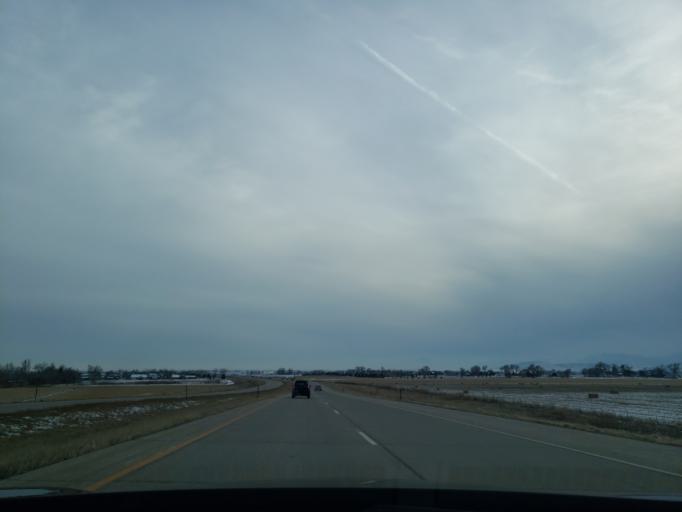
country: US
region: Colorado
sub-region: Larimer County
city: Berthoud
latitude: 40.3201
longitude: -105.1037
